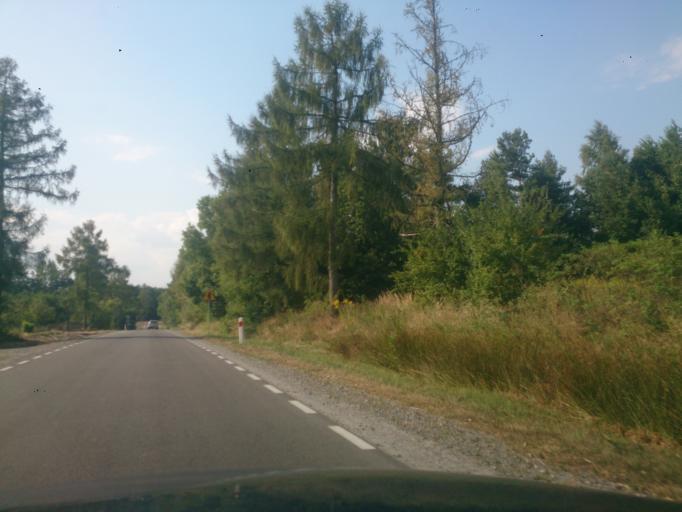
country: PL
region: Swietokrzyskie
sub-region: Powiat opatowski
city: Iwaniska
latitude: 50.6962
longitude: 21.3383
